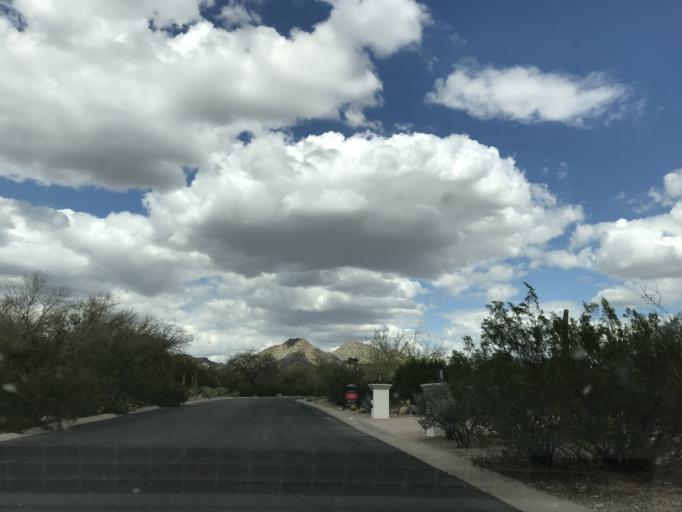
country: US
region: Arizona
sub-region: Maricopa County
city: Paradise Valley
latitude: 33.5182
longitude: -112.0019
